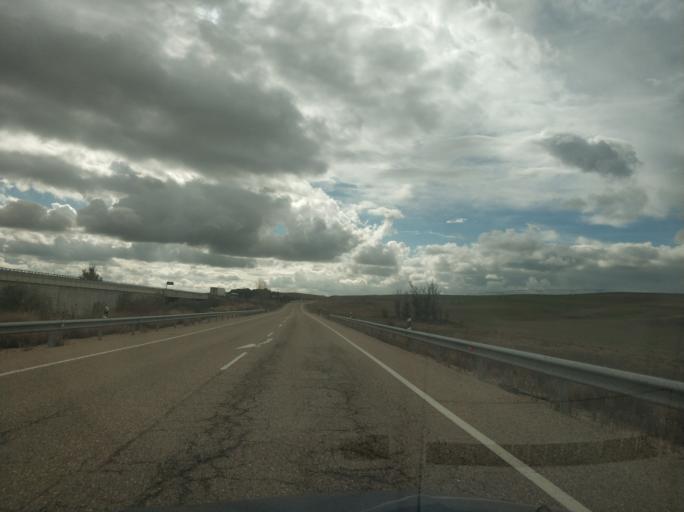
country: ES
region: Castille and Leon
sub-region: Provincia de Valladolid
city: Torrecilla de la Abadesa
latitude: 41.4492
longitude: -5.0894
